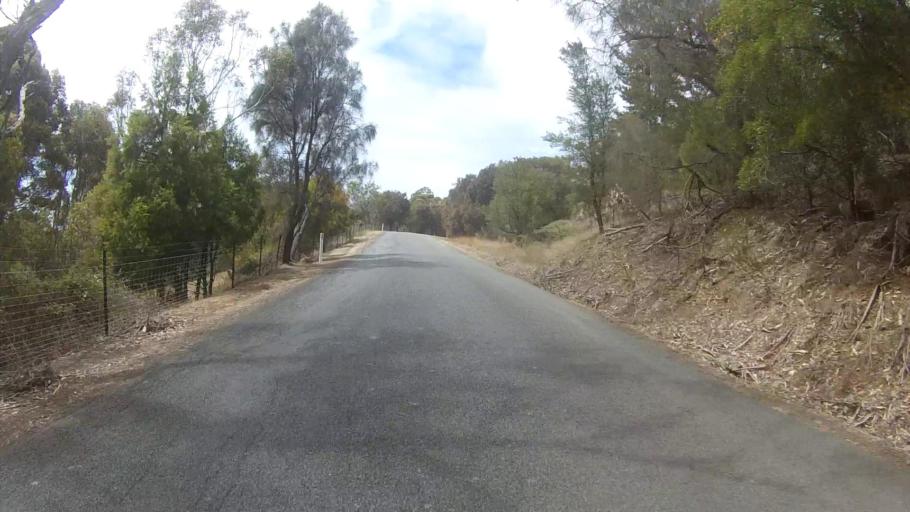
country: AU
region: Tasmania
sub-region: Kingborough
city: Blackmans Bay
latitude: -43.0437
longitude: 147.3336
